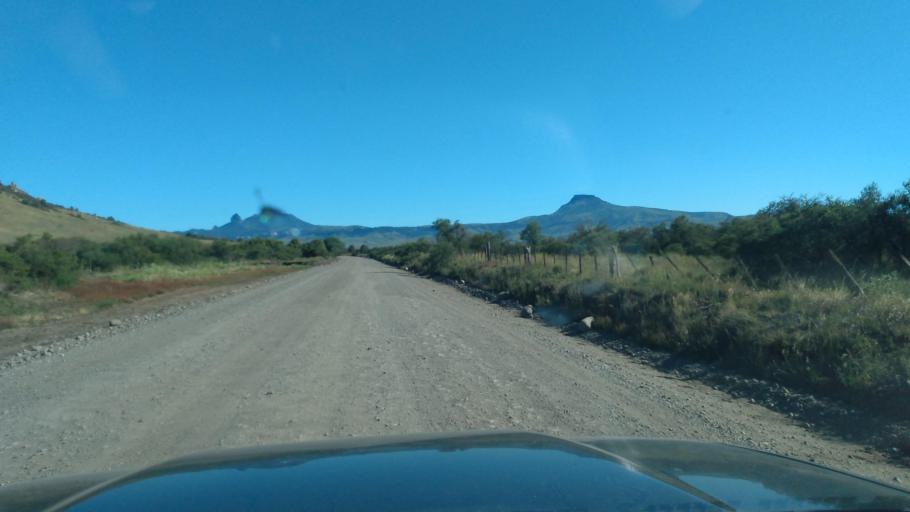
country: AR
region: Neuquen
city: Junin de los Andes
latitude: -39.8434
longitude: -71.1885
